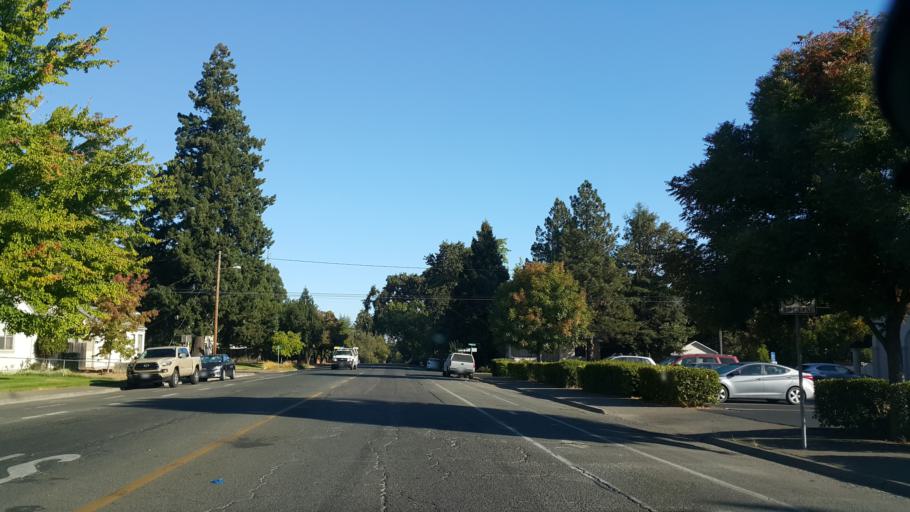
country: US
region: California
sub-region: Mendocino County
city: Ukiah
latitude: 39.1493
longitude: -123.2124
